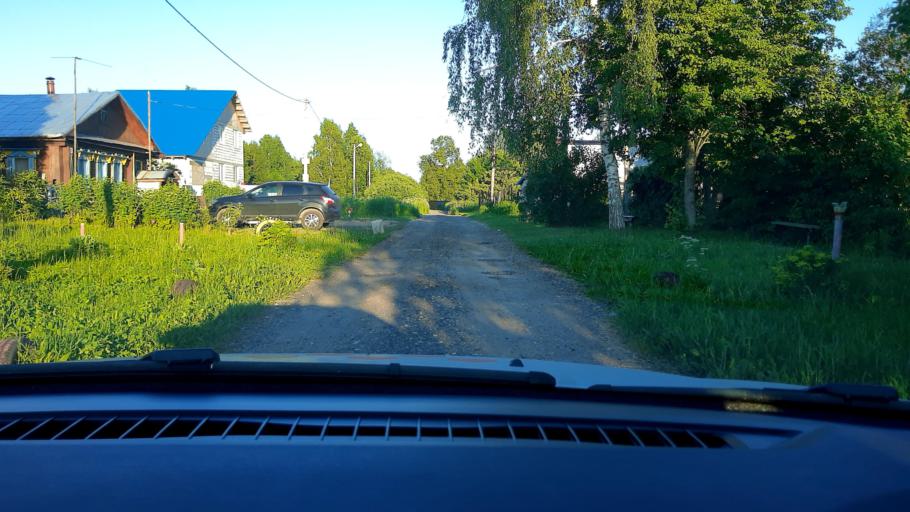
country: RU
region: Nizjnij Novgorod
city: Kstovo
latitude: 56.3092
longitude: 44.2715
